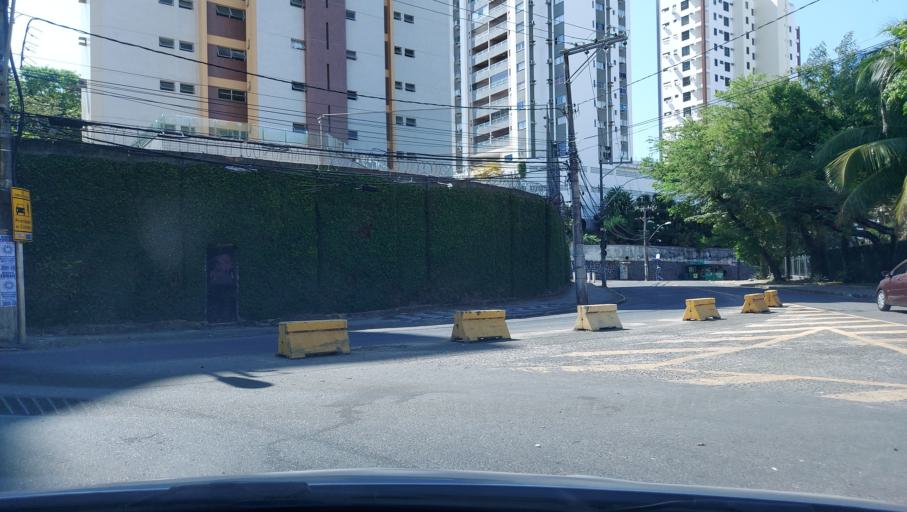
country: BR
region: Bahia
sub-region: Salvador
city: Salvador
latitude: -12.9897
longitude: -38.4668
